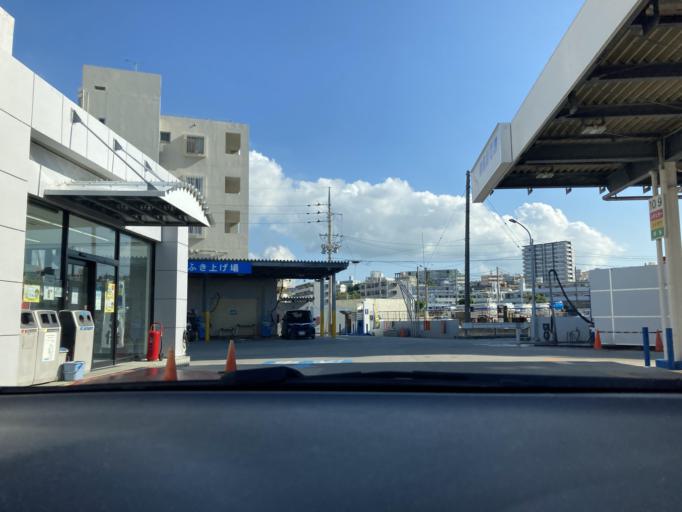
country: JP
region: Okinawa
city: Tomigusuku
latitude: 26.1953
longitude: 127.7268
